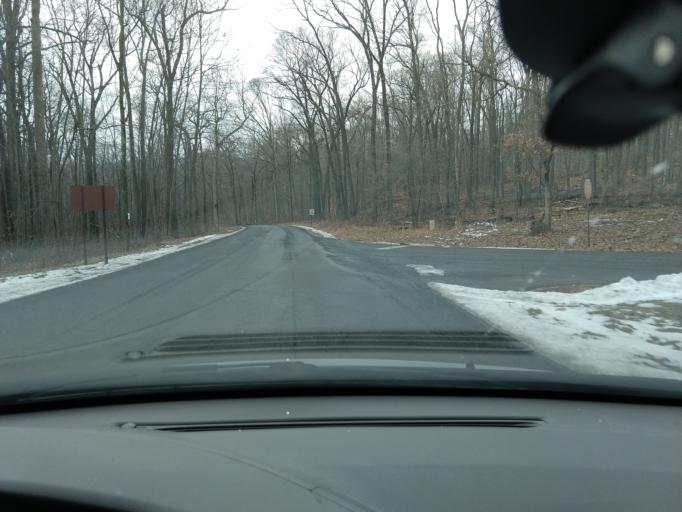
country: US
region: Pennsylvania
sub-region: Berks County
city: Birdsboro
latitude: 40.2081
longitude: -75.7881
